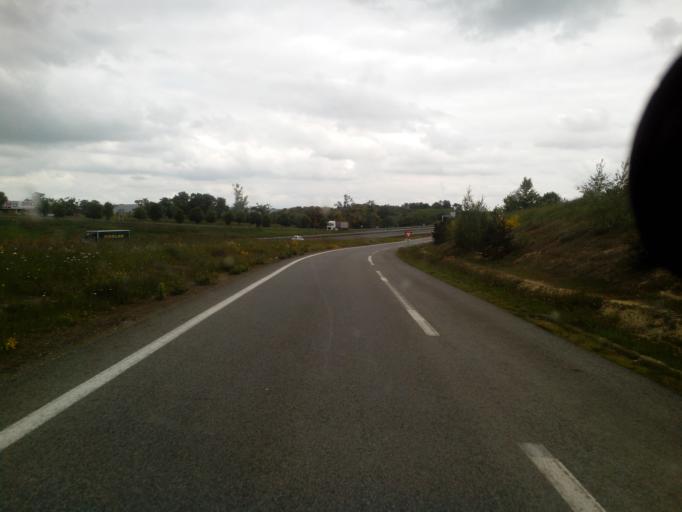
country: FR
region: Brittany
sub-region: Departement d'Ille-et-Vilaine
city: Liffre
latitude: 48.2213
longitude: -1.4981
